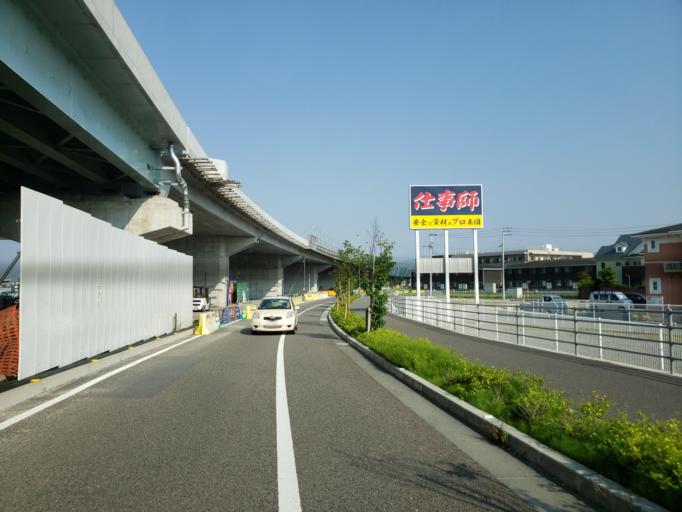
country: JP
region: Ehime
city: Masaki-cho
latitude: 33.8190
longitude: 132.7177
